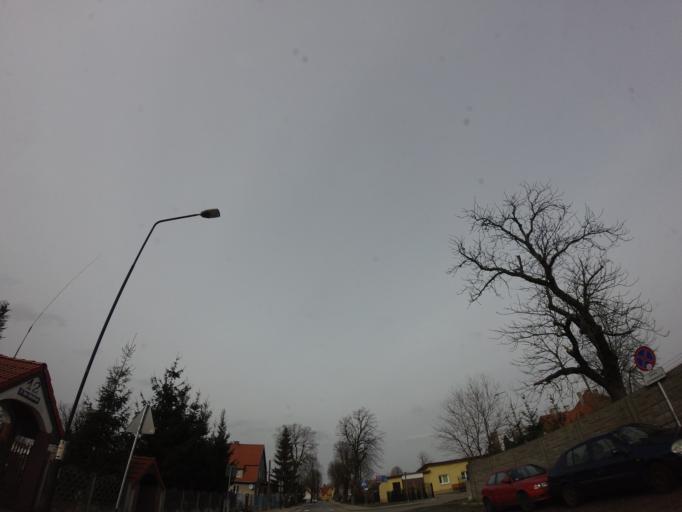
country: PL
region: West Pomeranian Voivodeship
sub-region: Powiat drawski
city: Drawsko Pomorskie
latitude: 53.5223
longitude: 15.8163
